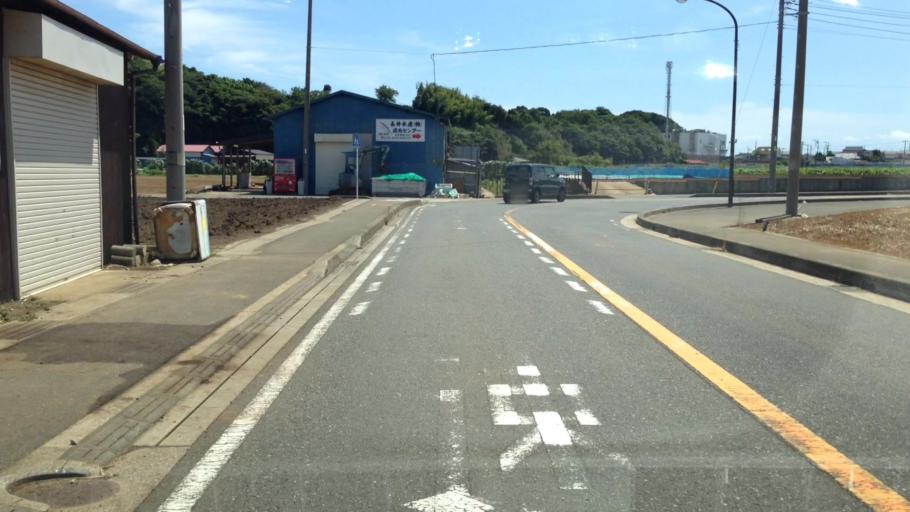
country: JP
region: Kanagawa
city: Miura
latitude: 35.1972
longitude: 139.6190
